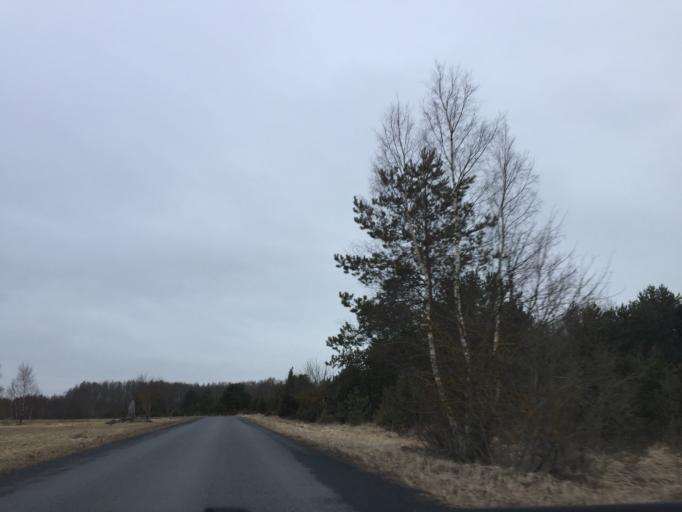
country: EE
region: Laeaene
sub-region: Haapsalu linn
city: Haapsalu
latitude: 58.7942
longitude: 23.4836
